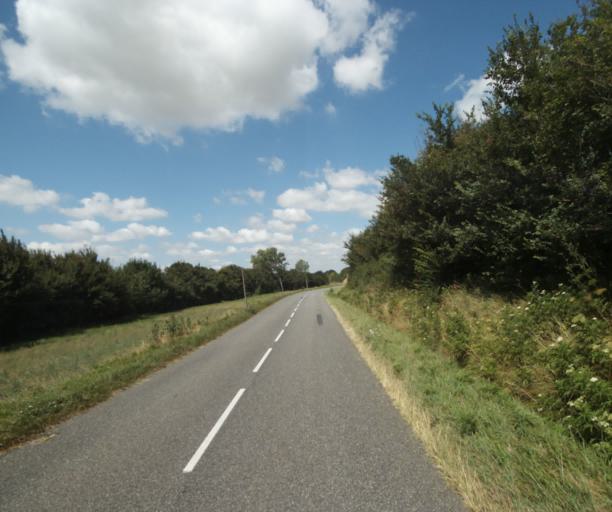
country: FR
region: Midi-Pyrenees
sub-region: Departement de la Haute-Garonne
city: Auriac-sur-Vendinelle
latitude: 43.4791
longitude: 1.8023
